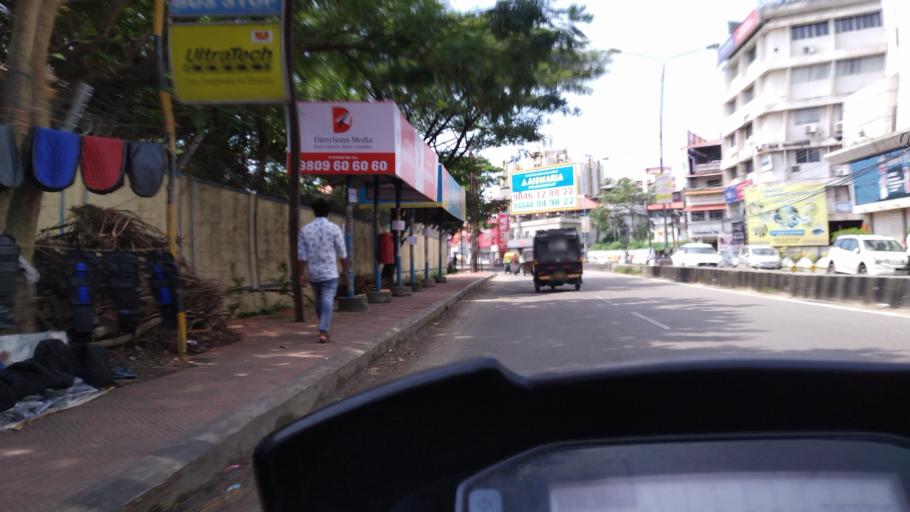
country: IN
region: Kerala
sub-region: Ernakulam
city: Cochin
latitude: 9.9560
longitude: 76.2920
